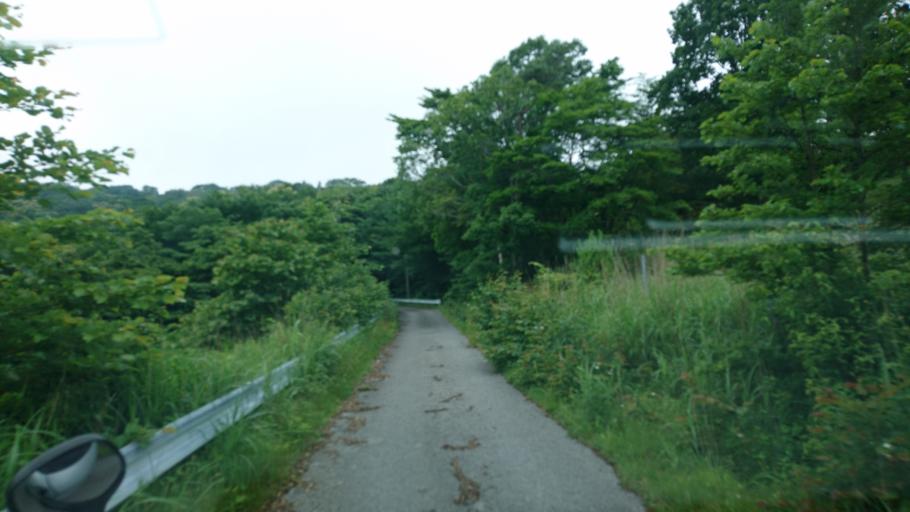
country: JP
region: Iwate
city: Ofunato
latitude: 39.1747
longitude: 141.7636
